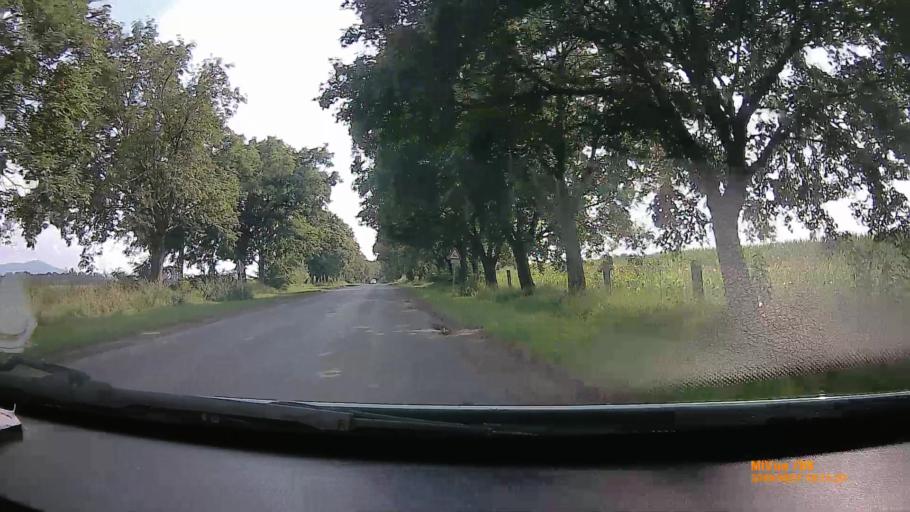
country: HU
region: Borsod-Abauj-Zemplen
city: Gonc
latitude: 48.4702
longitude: 21.2555
